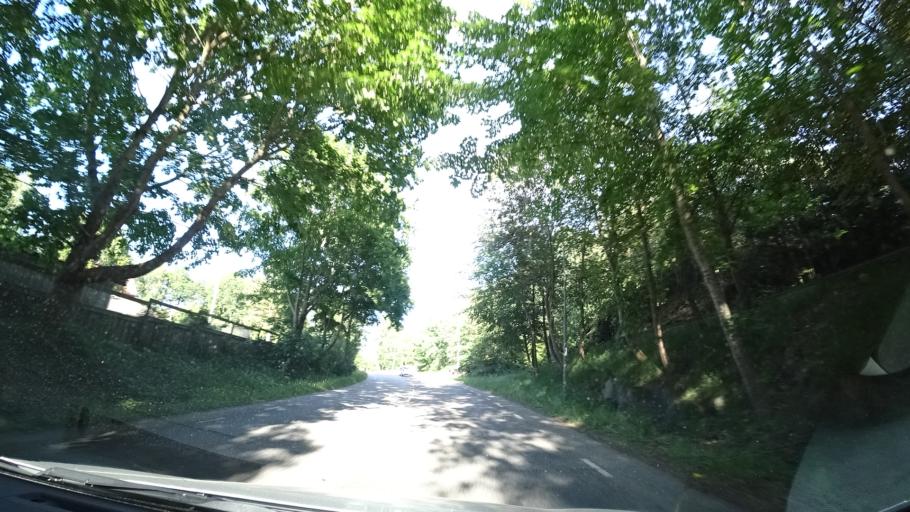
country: SE
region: Vaestra Goetaland
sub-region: Goteborg
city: Billdal
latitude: 57.5881
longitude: 11.9419
